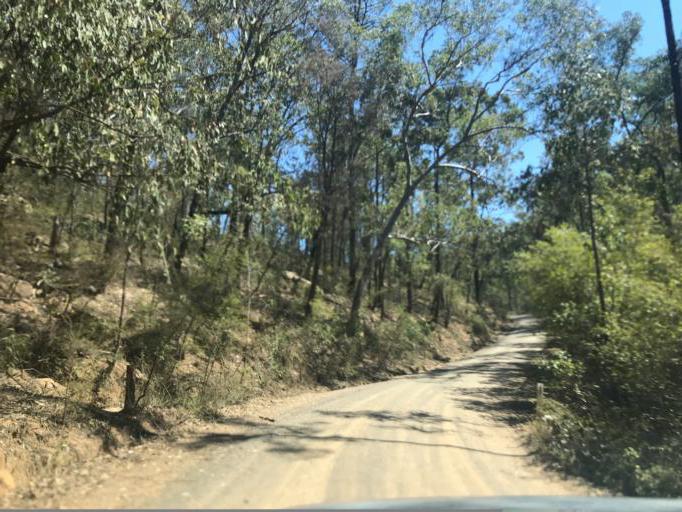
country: AU
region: New South Wales
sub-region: Wyong Shire
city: Little Jilliby
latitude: -33.1868
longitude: 151.0540
